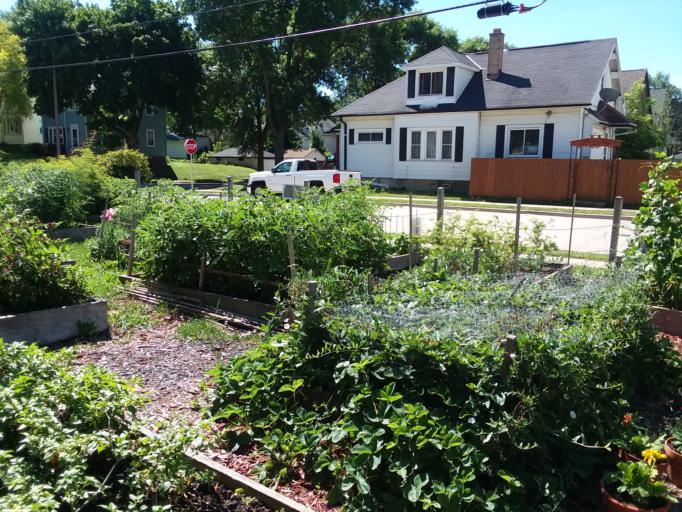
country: US
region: Wisconsin
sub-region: Milwaukee County
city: Milwaukee
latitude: 42.9969
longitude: -87.9085
